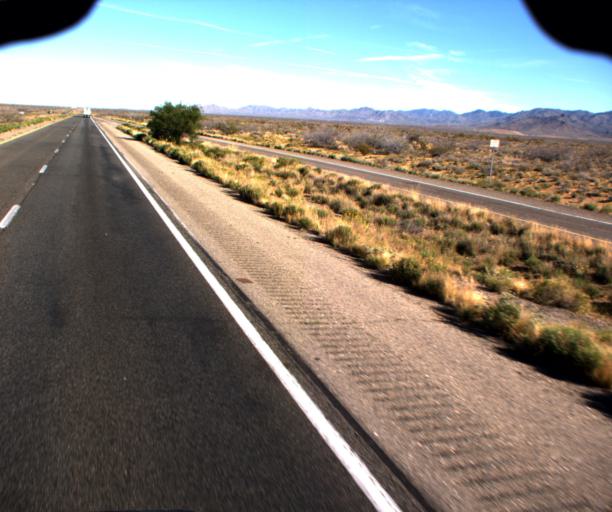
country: US
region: Arizona
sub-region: Mohave County
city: Golden Valley
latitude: 35.2971
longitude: -114.1869
